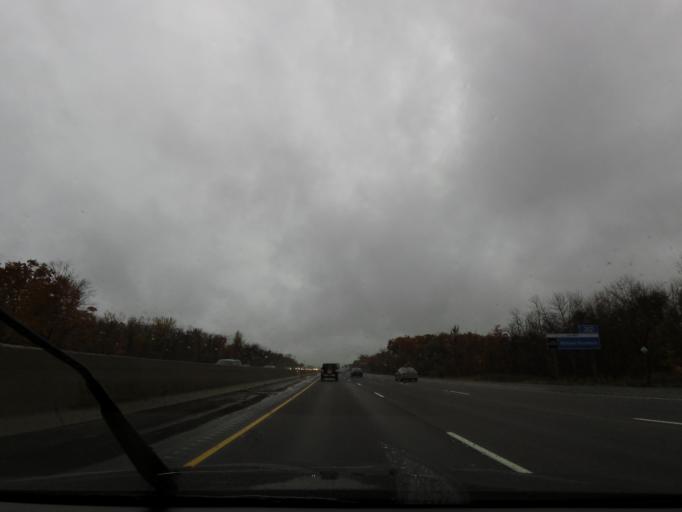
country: CA
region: Ontario
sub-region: Halton
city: Milton
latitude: 43.4735
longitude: -80.0352
